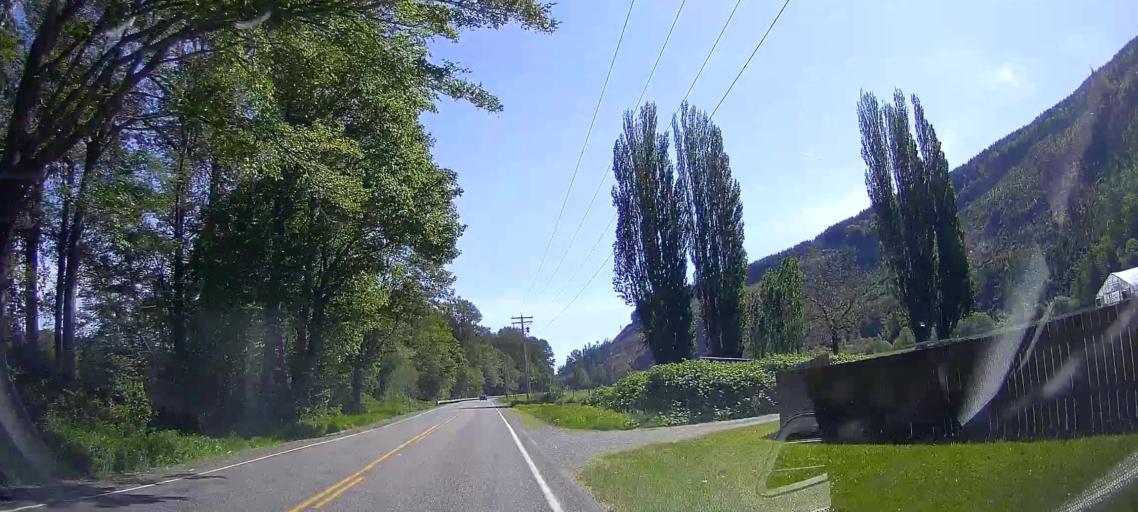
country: US
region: Washington
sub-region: Skagit County
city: Sedro-Woolley
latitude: 48.4860
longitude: -122.2343
